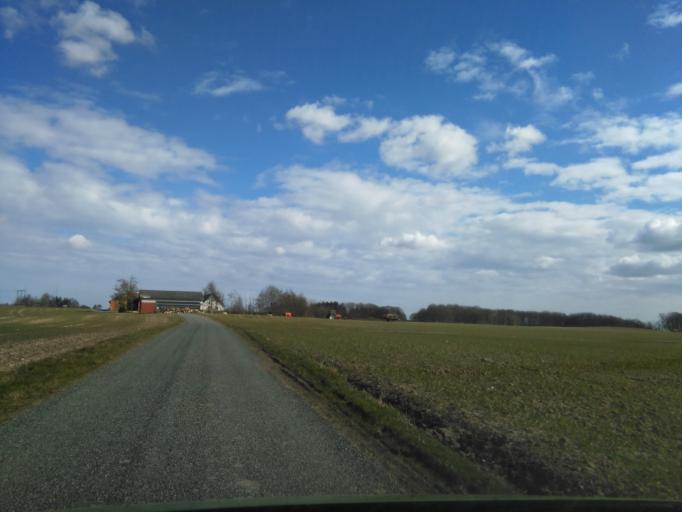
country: DK
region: Central Jutland
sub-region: Skanderborg Kommune
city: Stilling
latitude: 55.9199
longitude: 10.0061
